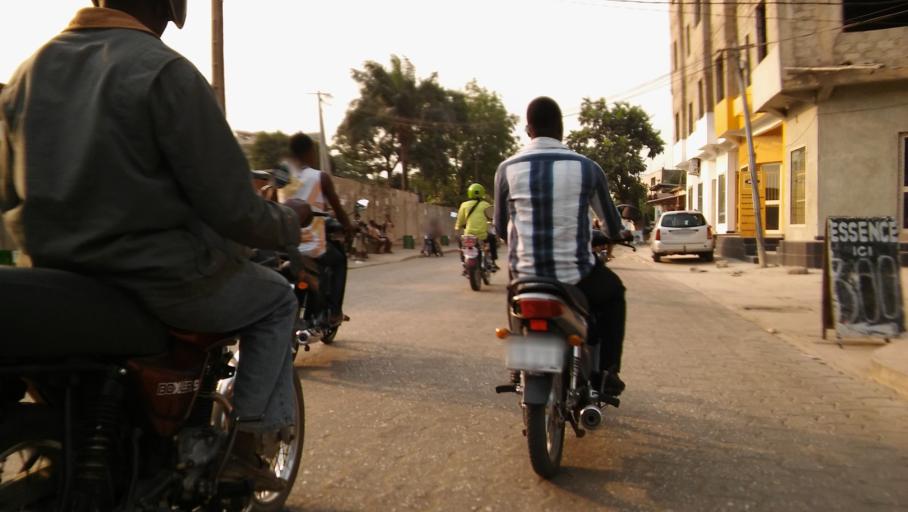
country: BJ
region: Littoral
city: Cotonou
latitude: 6.3822
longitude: 2.3884
